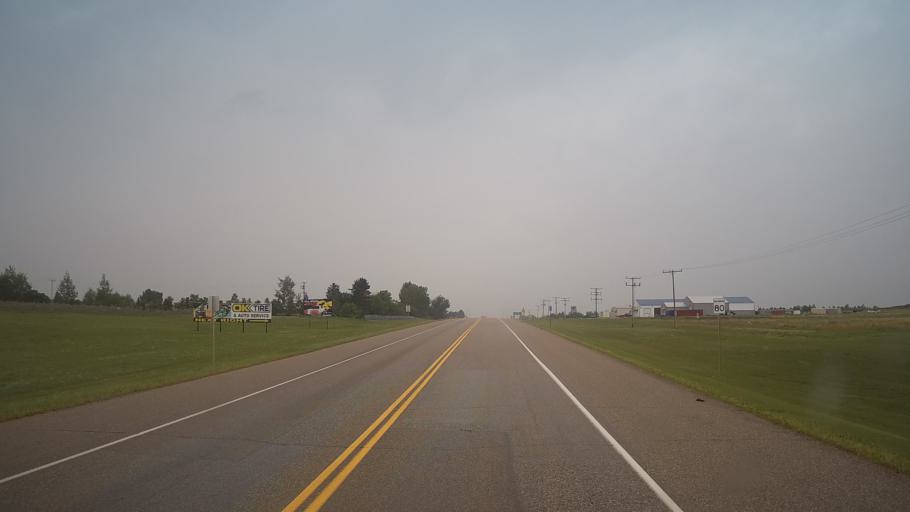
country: CA
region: Saskatchewan
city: Biggar
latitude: 52.0606
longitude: -107.9705
